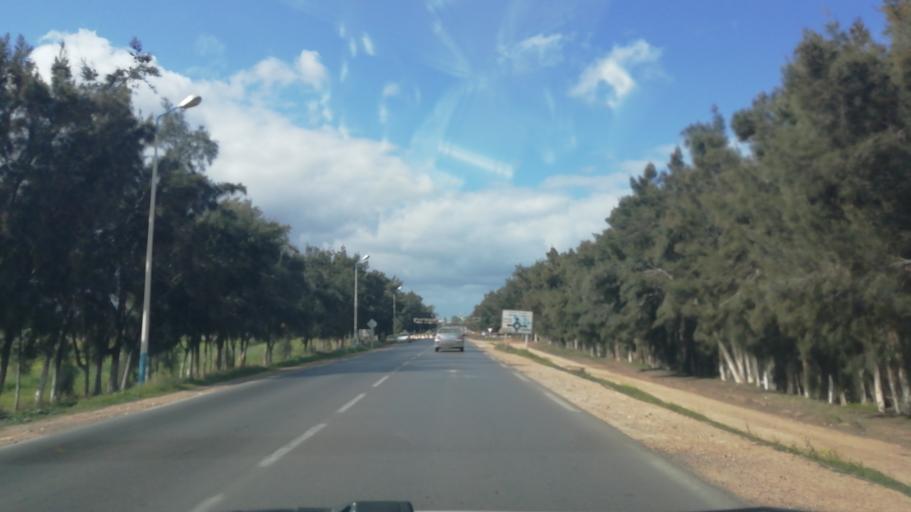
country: DZ
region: Relizane
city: Mazouna
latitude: 36.2558
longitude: 0.5842
